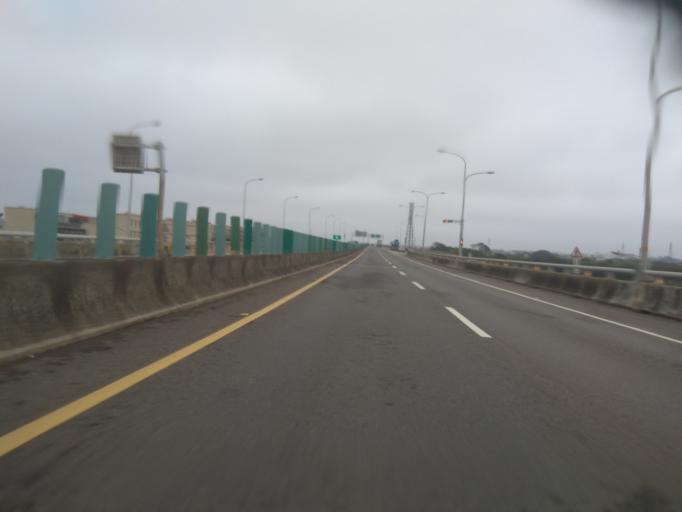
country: TW
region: Taiwan
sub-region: Hsinchu
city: Zhubei
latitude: 24.9995
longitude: 121.1018
